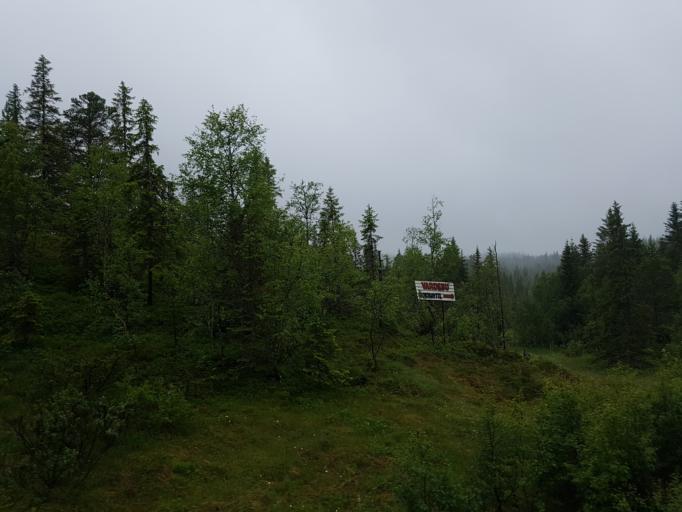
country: NO
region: Sor-Trondelag
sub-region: Selbu
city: Mebonden
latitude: 63.3394
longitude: 11.0804
